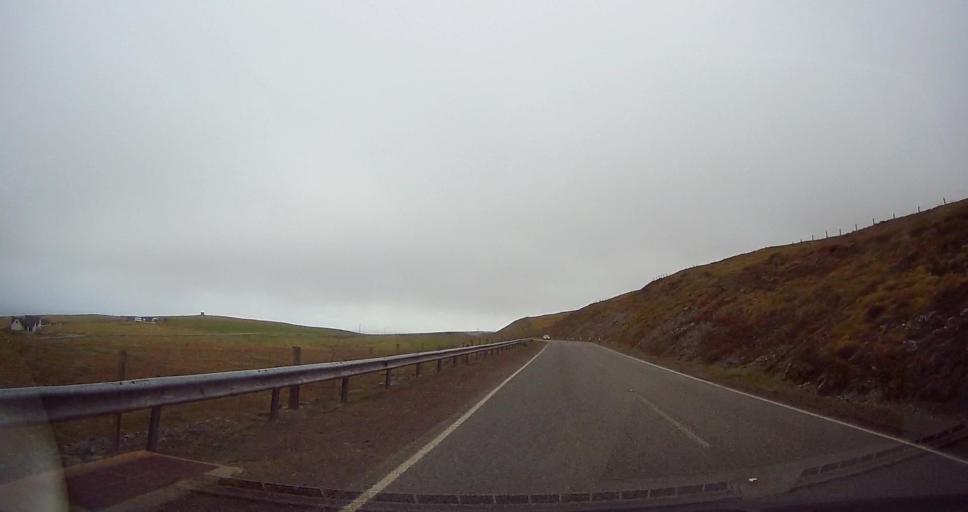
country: GB
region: Scotland
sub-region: Shetland Islands
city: Sandwick
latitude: 59.9672
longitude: -1.2809
